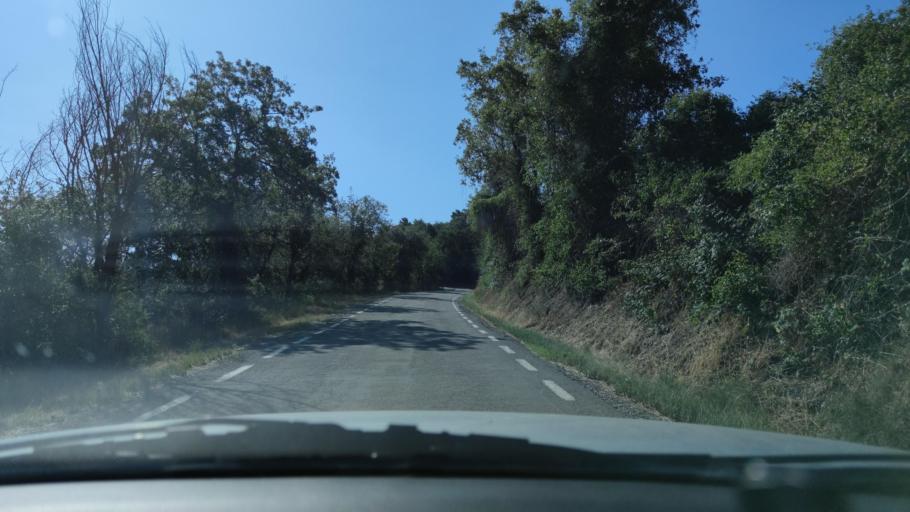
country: ES
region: Catalonia
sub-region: Provincia de Lleida
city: Ivorra
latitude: 41.7344
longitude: 1.3562
